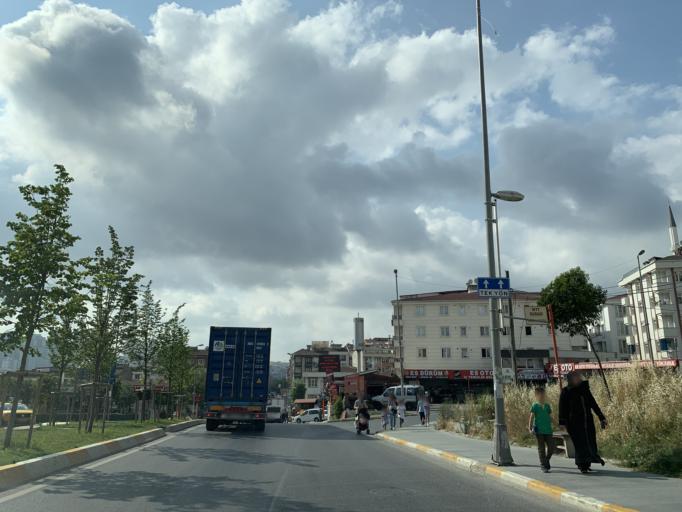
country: TR
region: Istanbul
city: Esenyurt
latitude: 41.0201
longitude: 28.6757
